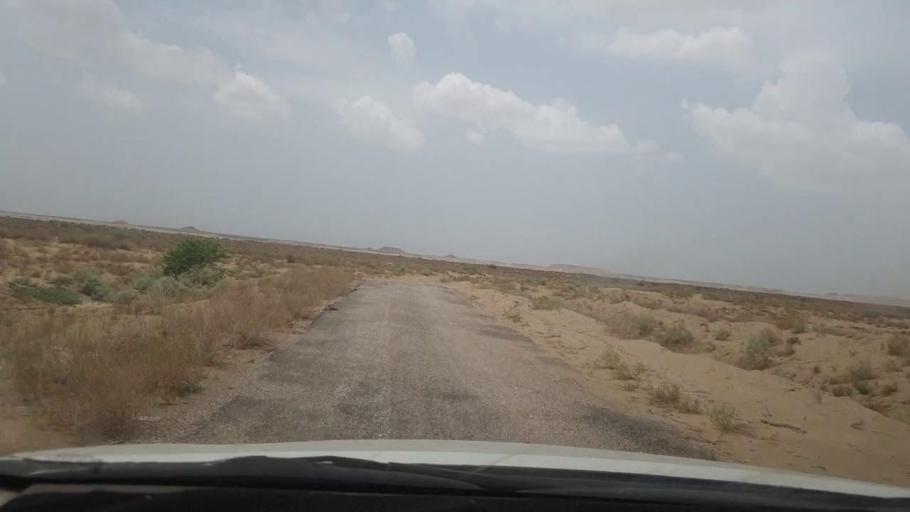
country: PK
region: Sindh
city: Khairpur
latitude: 27.4029
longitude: 68.9663
